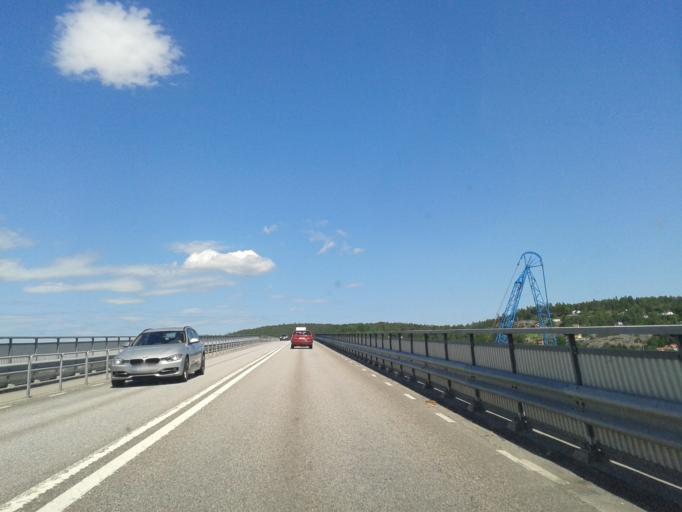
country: SE
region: Vaestra Goetaland
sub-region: Orust
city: Henan
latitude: 58.3034
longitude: 11.6997
